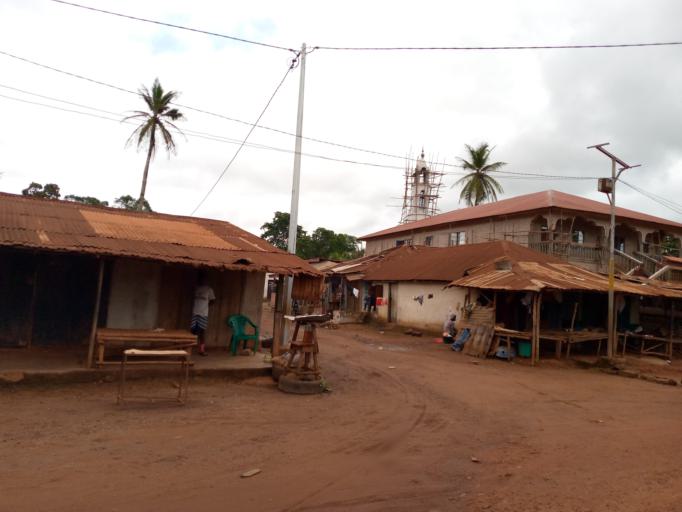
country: SL
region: Southern Province
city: Mogbwemo
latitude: 7.7868
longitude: -12.2973
